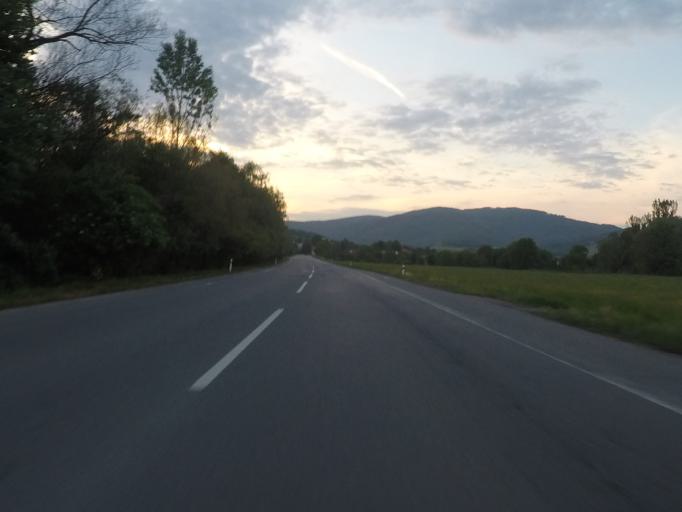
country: SK
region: Banskobystricky
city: Rimavska Sobota
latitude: 48.4957
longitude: 19.9392
